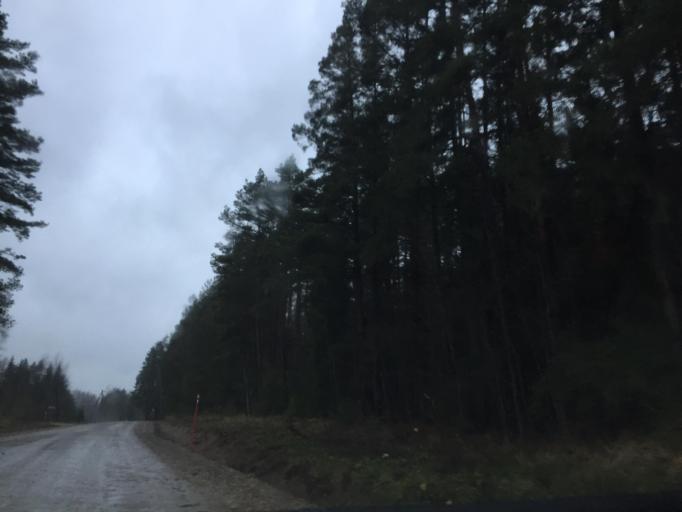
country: LV
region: Salacgrivas
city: Salacgriva
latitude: 57.7702
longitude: 24.4912
